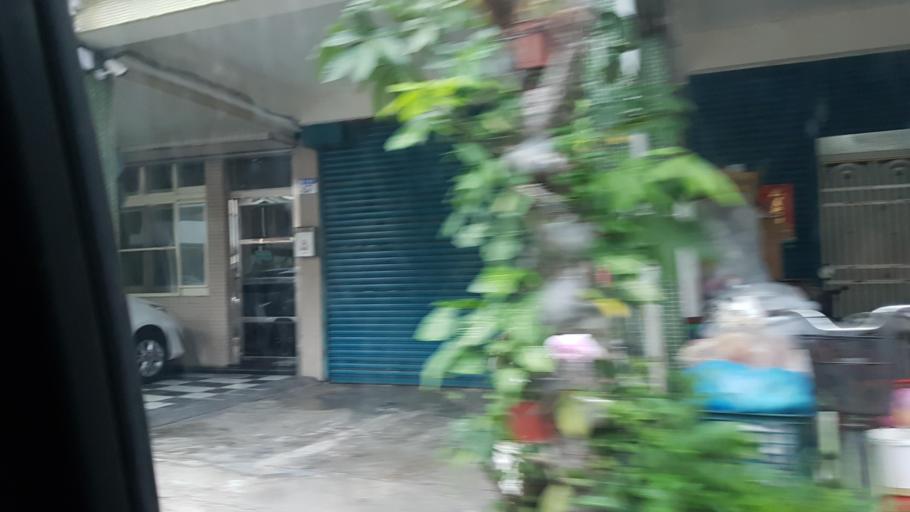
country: TW
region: Taiwan
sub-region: Hualien
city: Hualian
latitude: 23.9800
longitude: 121.5973
